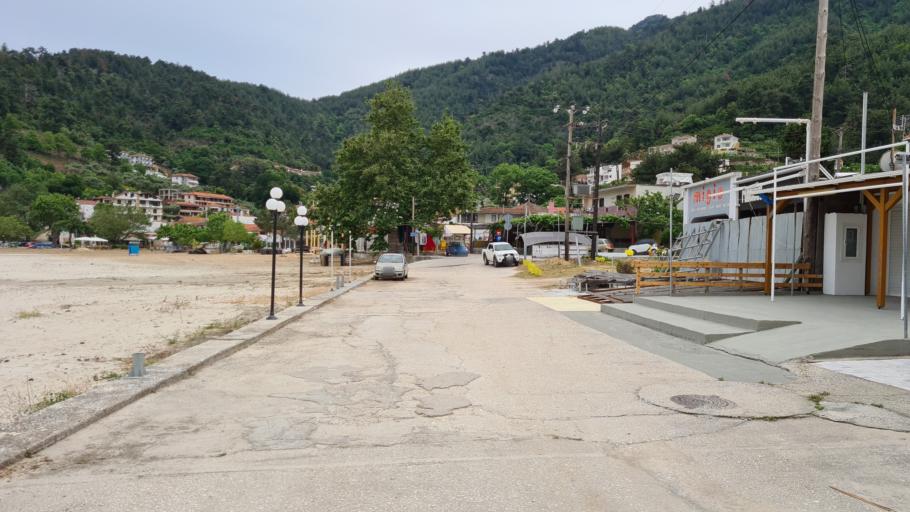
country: GR
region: East Macedonia and Thrace
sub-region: Nomos Kavalas
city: Potamia
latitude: 40.7095
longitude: 24.7596
